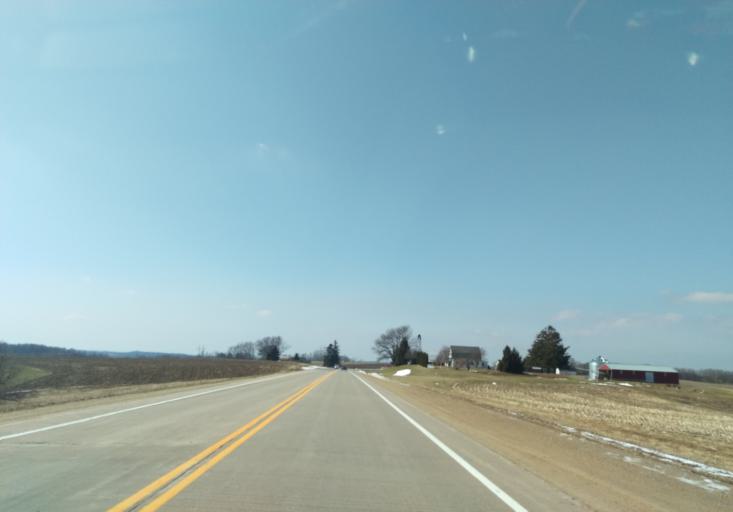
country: US
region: Wisconsin
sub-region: La Crosse County
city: La Crosse
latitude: 43.7321
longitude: -91.0989
